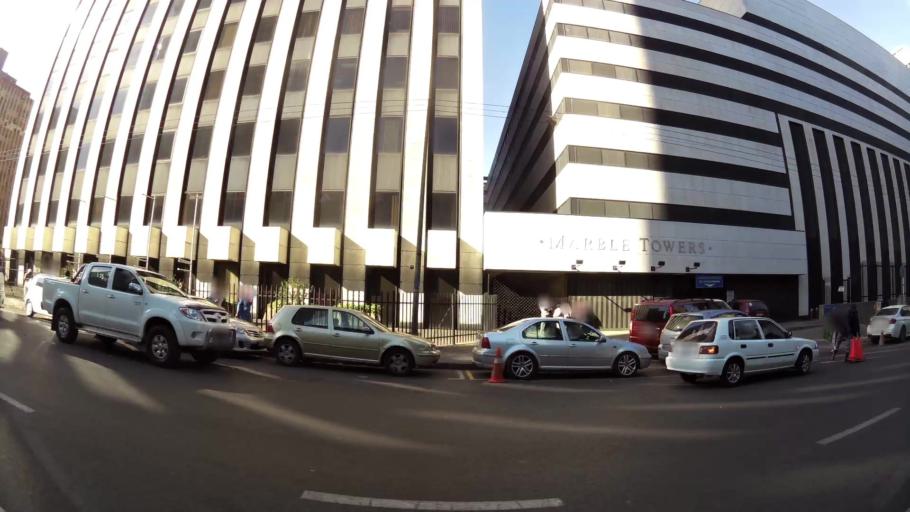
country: ZA
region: Gauteng
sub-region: City of Johannesburg Metropolitan Municipality
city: Johannesburg
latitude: -26.2022
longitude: 28.0472
